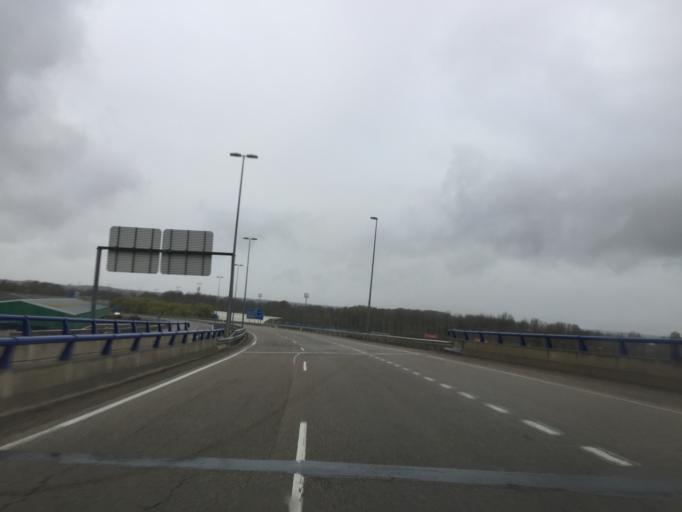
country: ES
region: Castille and Leon
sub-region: Provincia de Leon
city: Leon
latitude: 42.5756
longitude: -5.5563
